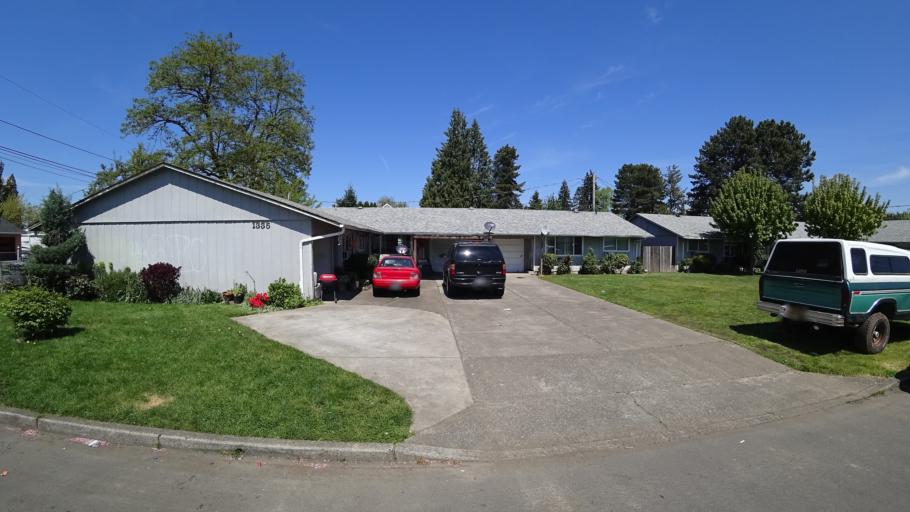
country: US
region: Oregon
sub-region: Washington County
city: Hillsboro
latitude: 45.5161
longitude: -122.9690
